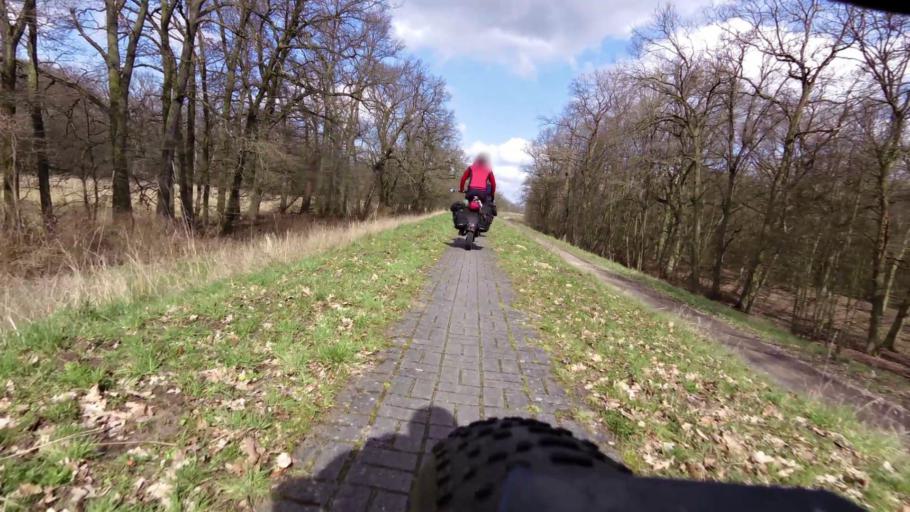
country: DE
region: Brandenburg
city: Lebus
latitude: 52.3954
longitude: 14.5407
